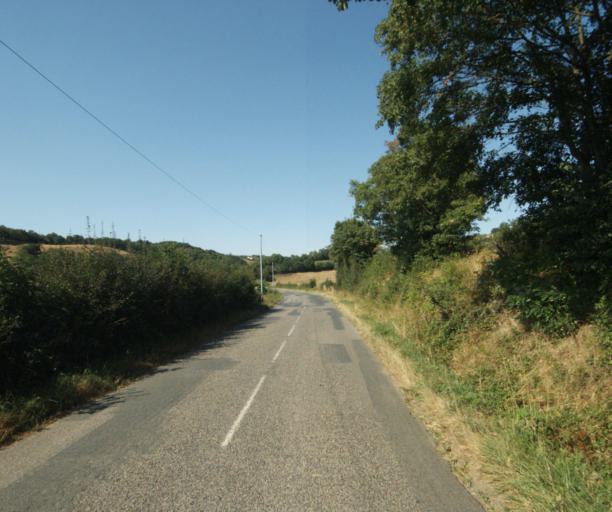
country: FR
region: Rhone-Alpes
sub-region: Departement du Rhone
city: Courzieu
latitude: 45.7602
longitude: 4.5639
